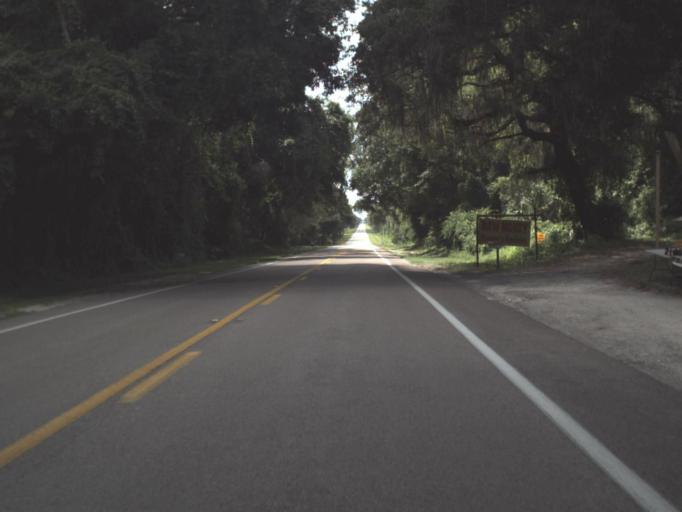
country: US
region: Florida
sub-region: Putnam County
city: East Palatka
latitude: 29.5978
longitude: -81.5731
